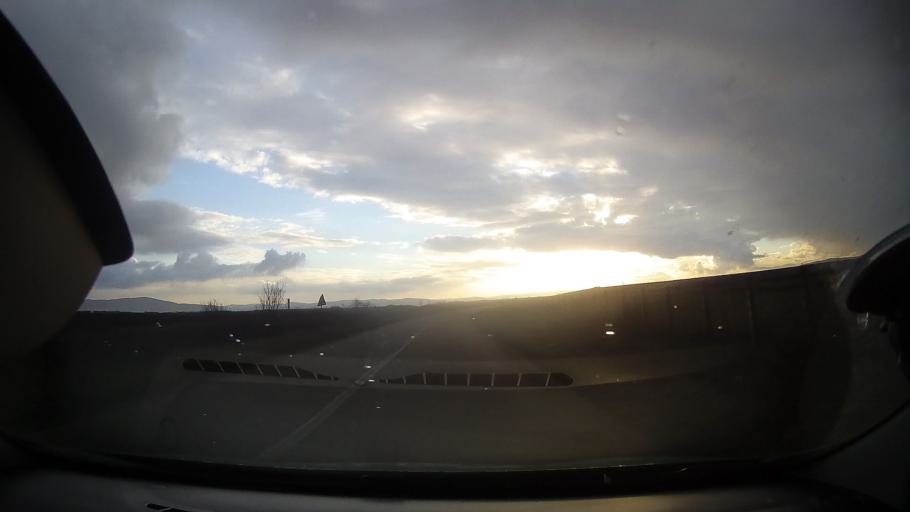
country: RO
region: Alba
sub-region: Comuna Lunca Muresului
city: Lunca Muresului
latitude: 46.4486
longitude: 23.9180
